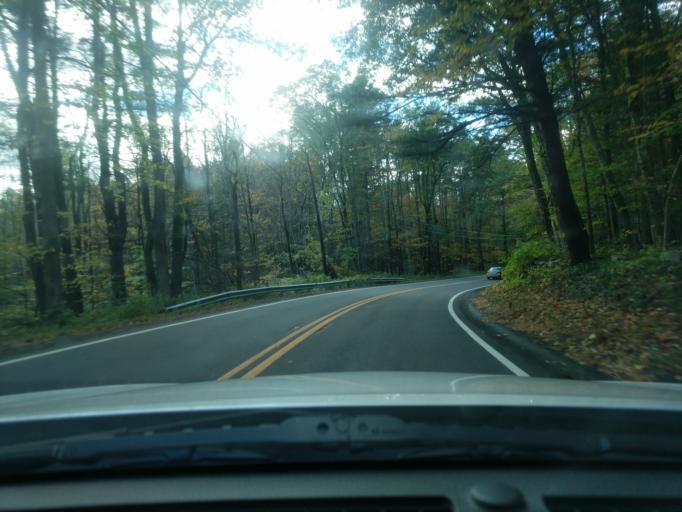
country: US
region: Massachusetts
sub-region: Berkshire County
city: Otis
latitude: 42.1929
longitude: -73.1217
